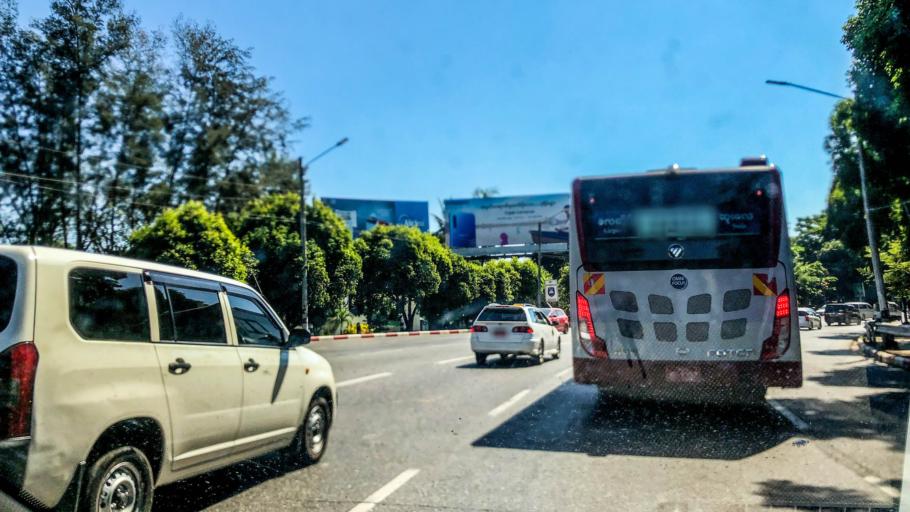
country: MM
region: Yangon
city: Yangon
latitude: 16.8848
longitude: 96.1358
